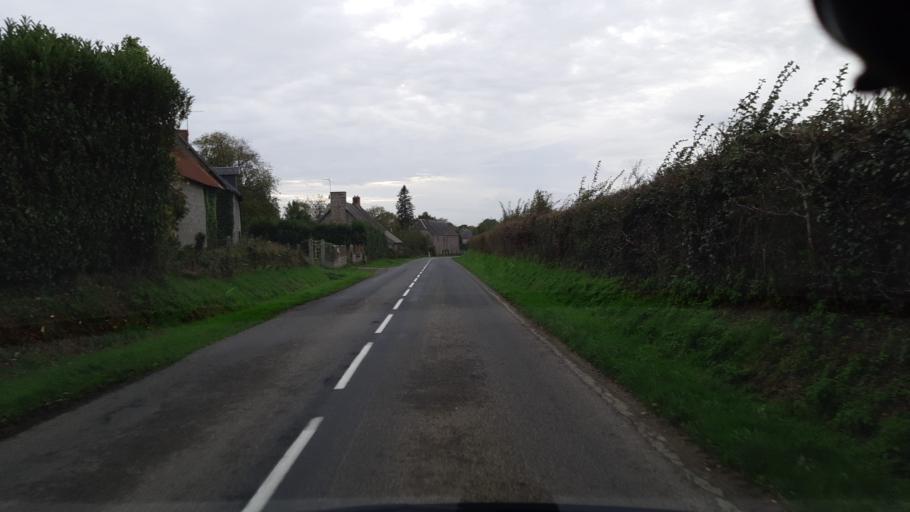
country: FR
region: Lower Normandy
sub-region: Departement de la Manche
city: Hambye
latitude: 48.9804
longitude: -1.2252
